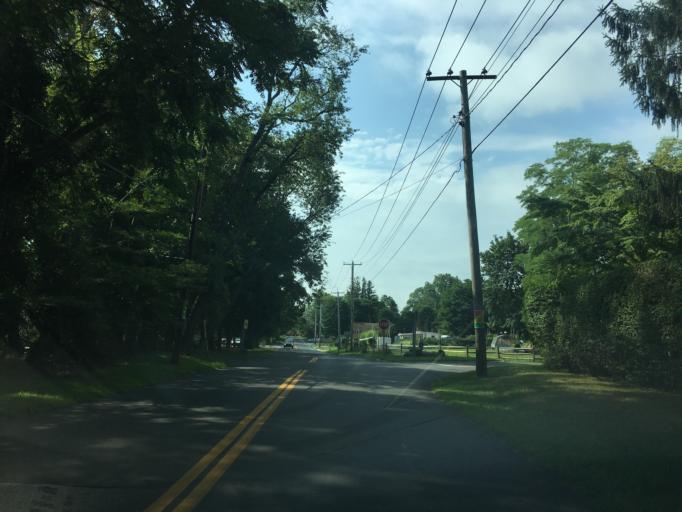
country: US
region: New York
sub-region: Suffolk County
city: Shelter Island
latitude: 41.0684
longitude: -72.3320
